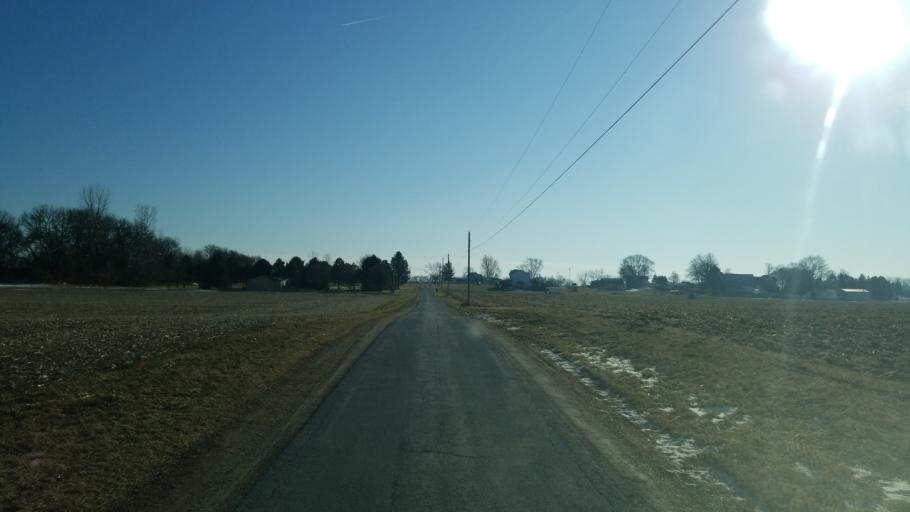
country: US
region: Ohio
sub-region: Sandusky County
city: Mount Carmel
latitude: 41.2747
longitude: -82.9415
